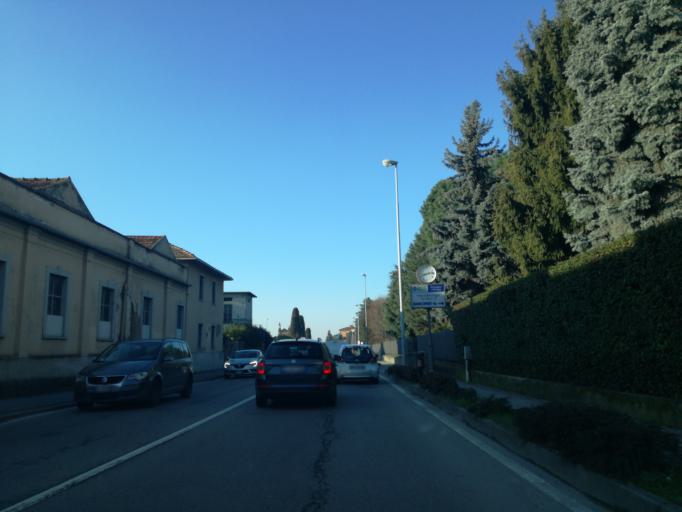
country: IT
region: Lombardy
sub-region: Provincia di Monza e Brianza
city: Bernareggio
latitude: 45.6465
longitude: 9.4052
